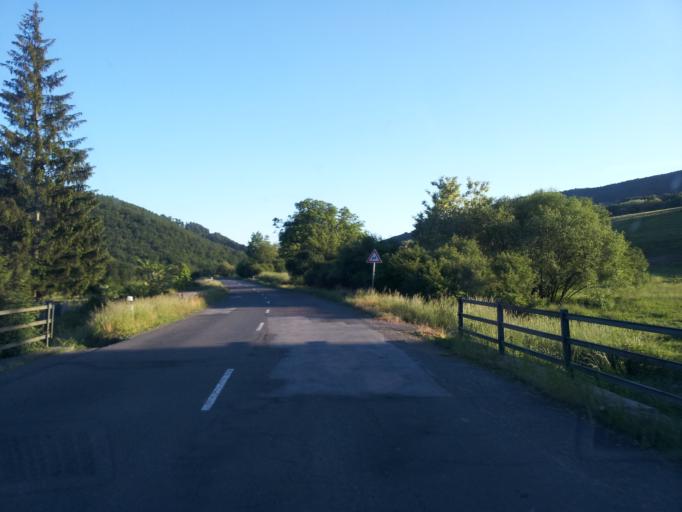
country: SK
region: Banskobystricky
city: Svaety Anton
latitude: 48.4032
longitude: 18.9398
